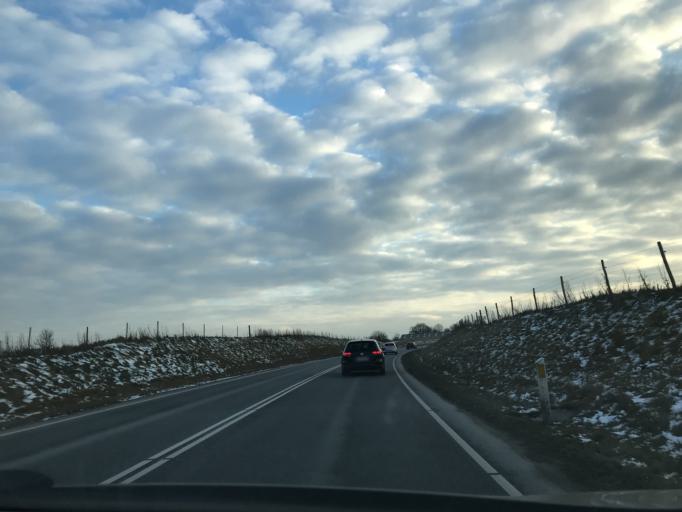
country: DK
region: Capital Region
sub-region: Egedal Kommune
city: Smorumnedre
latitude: 55.7237
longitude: 12.3152
